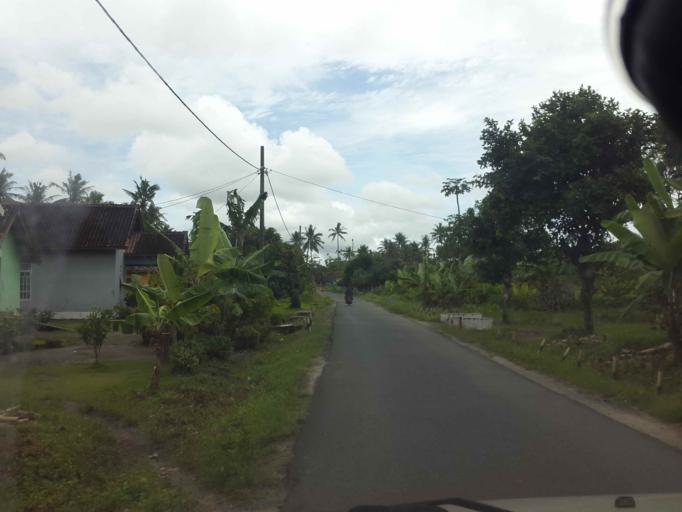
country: ID
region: Lampung
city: Sidorejo
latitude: -5.6489
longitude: 105.5801
